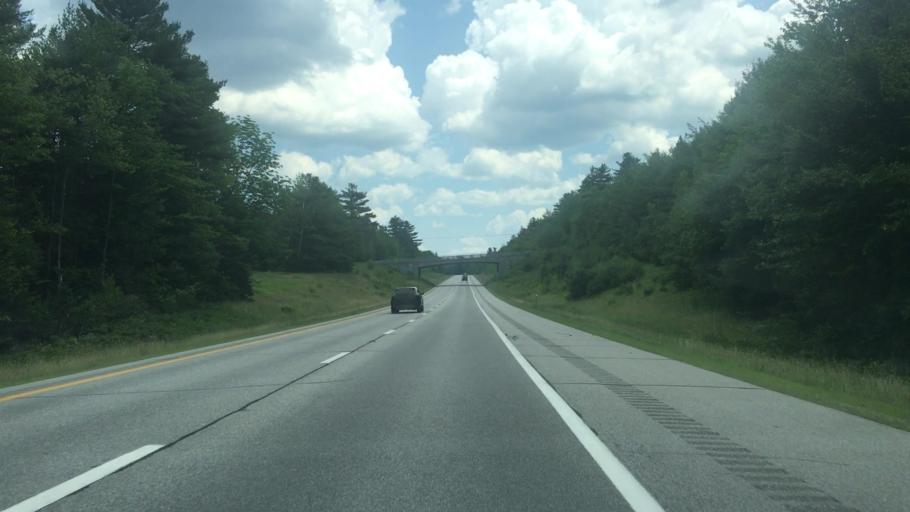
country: US
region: New Hampshire
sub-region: Merrimack County
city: New London
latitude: 43.4031
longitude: -72.0195
